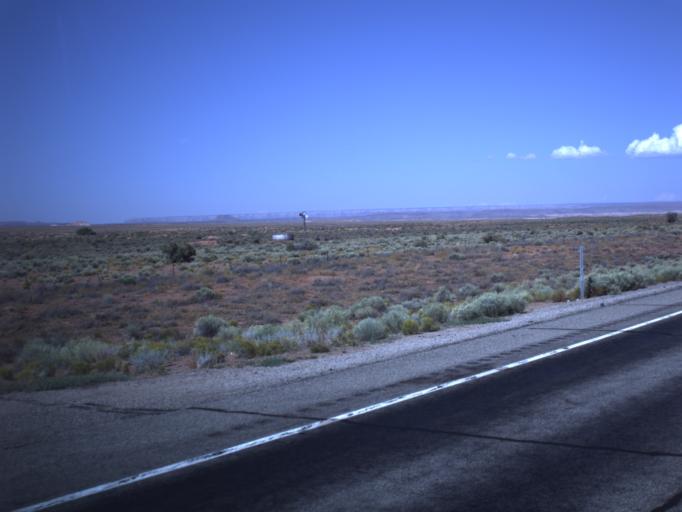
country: US
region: Utah
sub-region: San Juan County
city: Blanding
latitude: 37.1630
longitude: -109.5749
